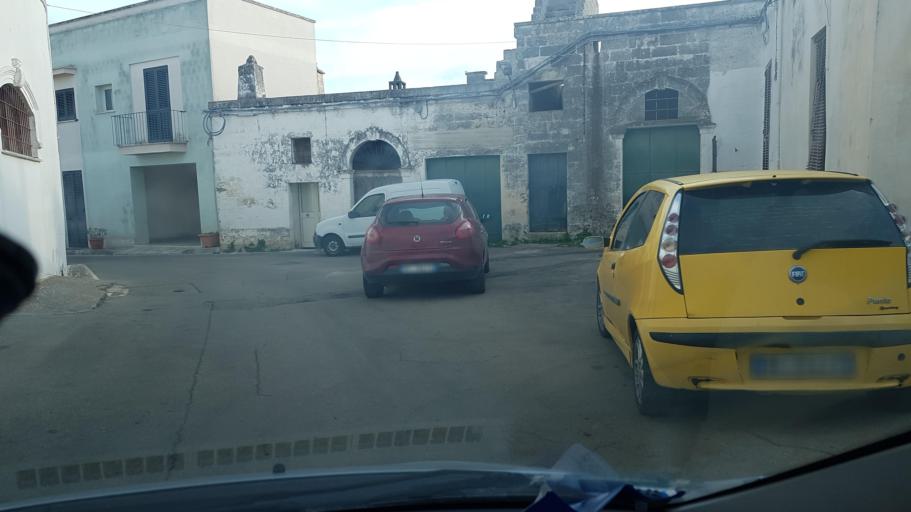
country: IT
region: Apulia
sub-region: Provincia di Lecce
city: Veglie
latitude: 40.3346
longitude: 17.9717
